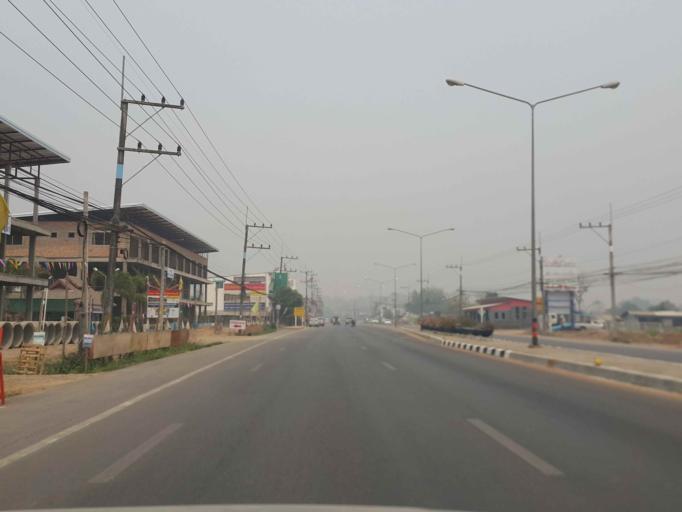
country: TH
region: Chiang Mai
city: Mae Taeng
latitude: 19.0887
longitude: 98.9368
